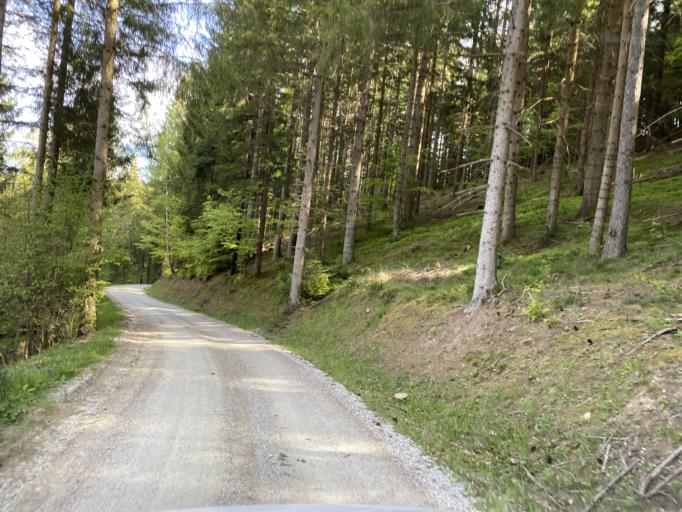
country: AT
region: Styria
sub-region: Politischer Bezirk Weiz
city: Gschaid bei Birkfeld
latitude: 47.3389
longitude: 15.7183
